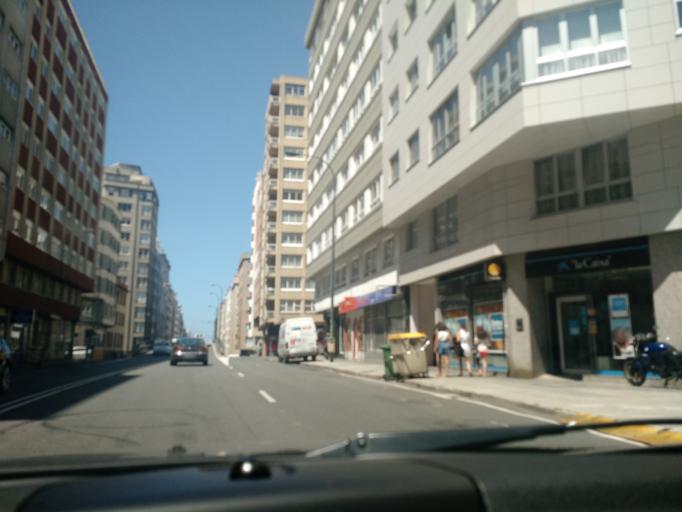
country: ES
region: Galicia
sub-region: Provincia da Coruna
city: A Coruna
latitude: 43.3604
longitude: -8.4149
